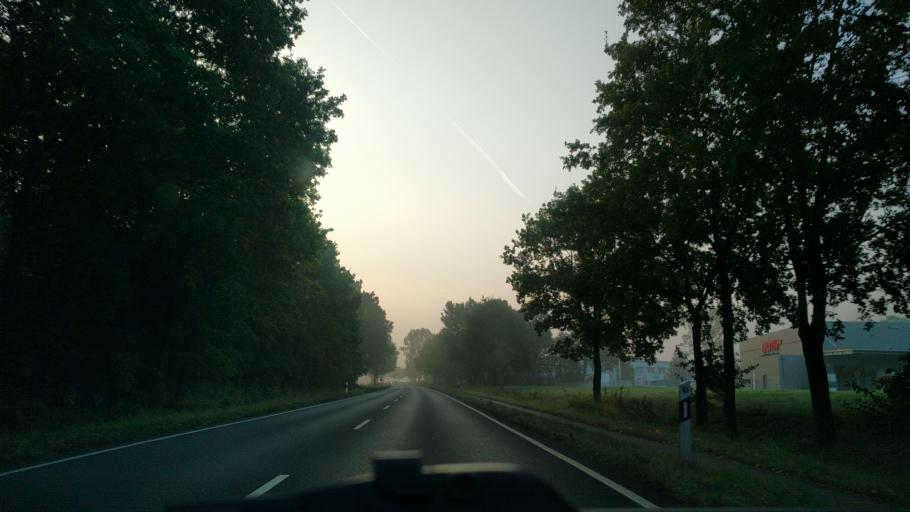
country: DE
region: Lower Saxony
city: Isenbuttel
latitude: 52.4459
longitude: 10.5915
